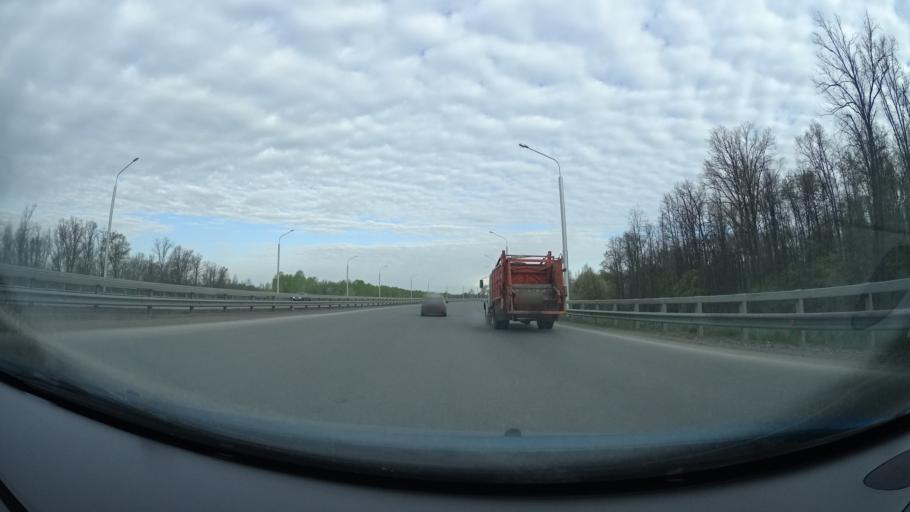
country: RU
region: Bashkortostan
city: Mikhaylovka
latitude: 54.7814
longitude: 55.9153
